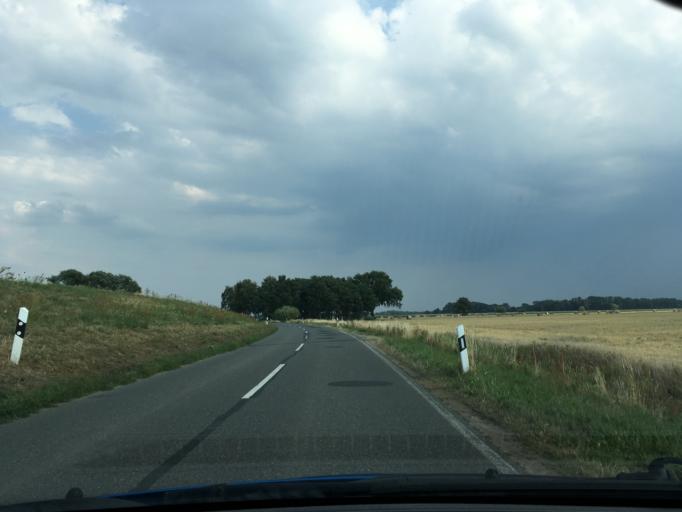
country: DE
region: Lower Saxony
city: Dannenberg
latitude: 53.1348
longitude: 11.0865
